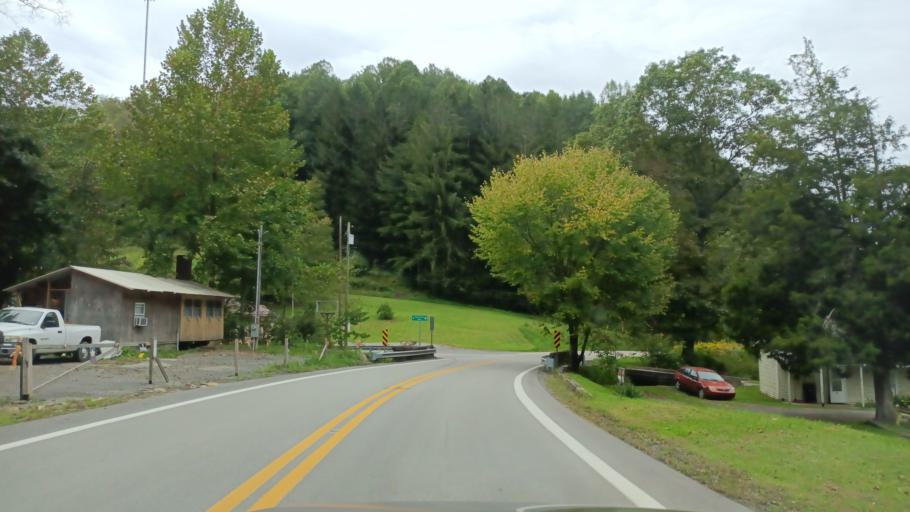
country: US
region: West Virginia
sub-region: Taylor County
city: Grafton
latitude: 39.3426
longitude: -79.9366
